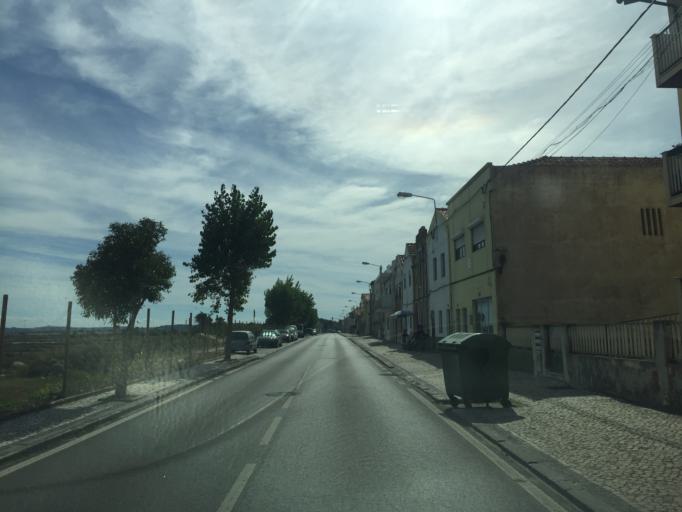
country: PT
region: Coimbra
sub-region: Figueira da Foz
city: Figueira da Foz
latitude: 40.1287
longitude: -8.8537
